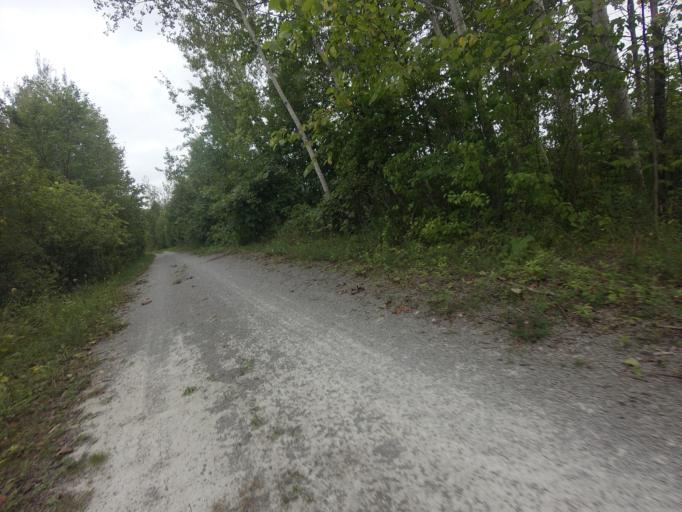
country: CA
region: Ontario
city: Uxbridge
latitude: 44.2996
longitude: -78.9246
